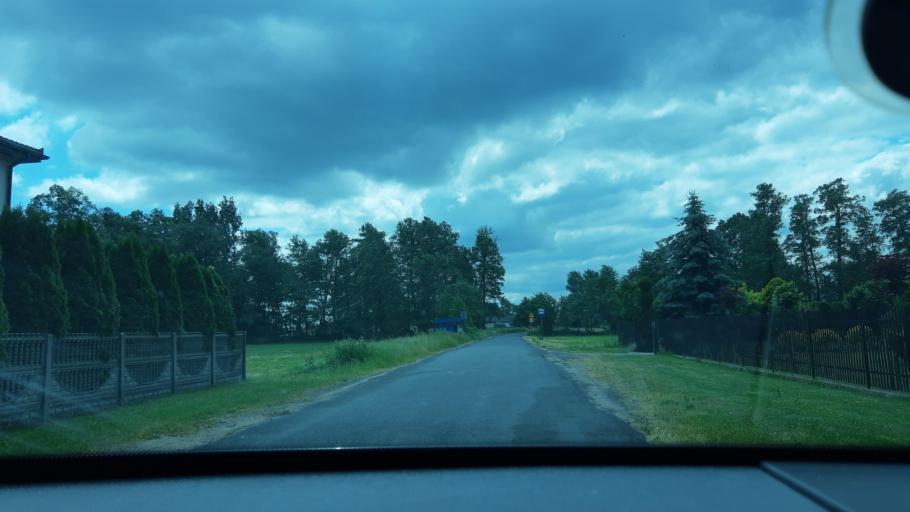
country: PL
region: Lodz Voivodeship
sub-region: Powiat zdunskowolski
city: Zapolice
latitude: 51.5293
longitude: 18.8379
